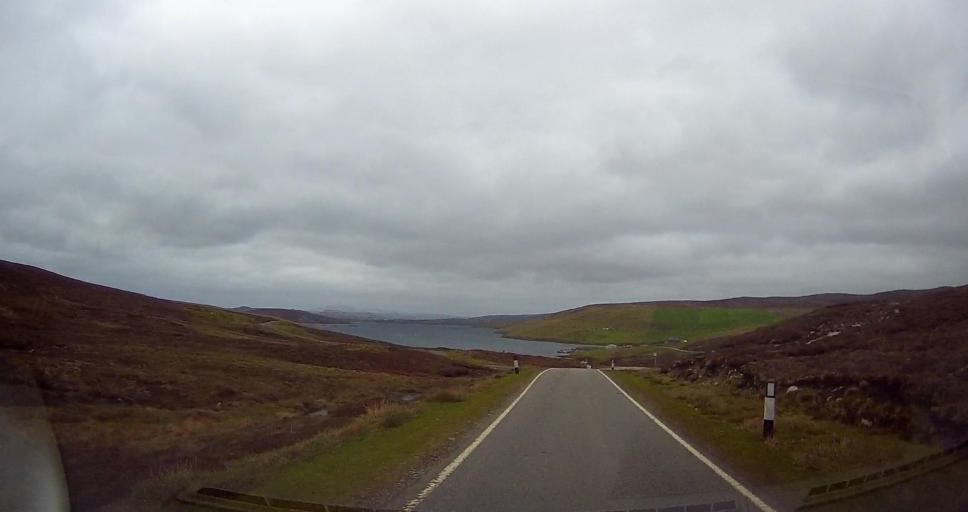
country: GB
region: Scotland
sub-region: Shetland Islands
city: Lerwick
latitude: 60.3273
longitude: -1.3385
